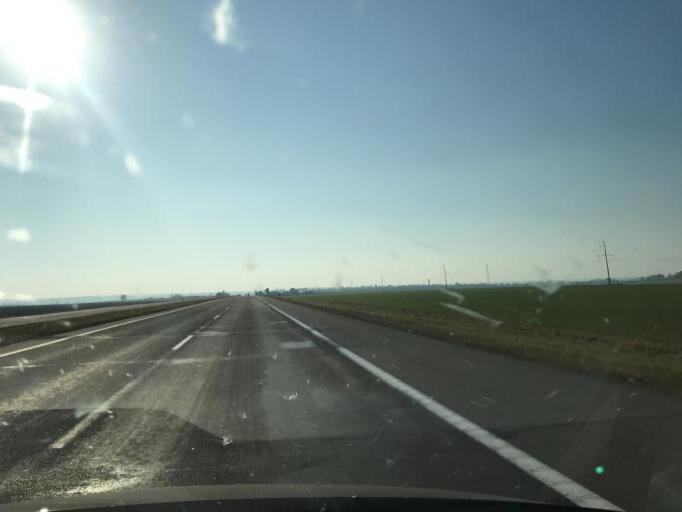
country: BY
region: Minsk
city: Haradzyeya
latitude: 53.3608
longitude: 26.4758
